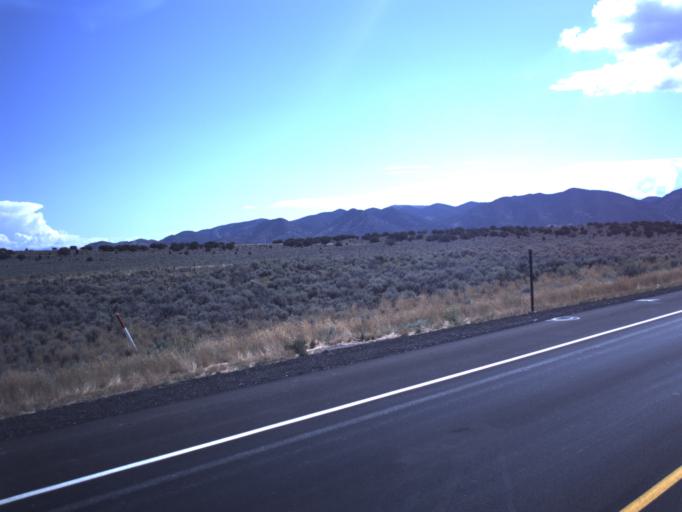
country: US
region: Utah
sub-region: Utah County
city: Eagle Mountain
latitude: 40.0548
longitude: -112.3014
